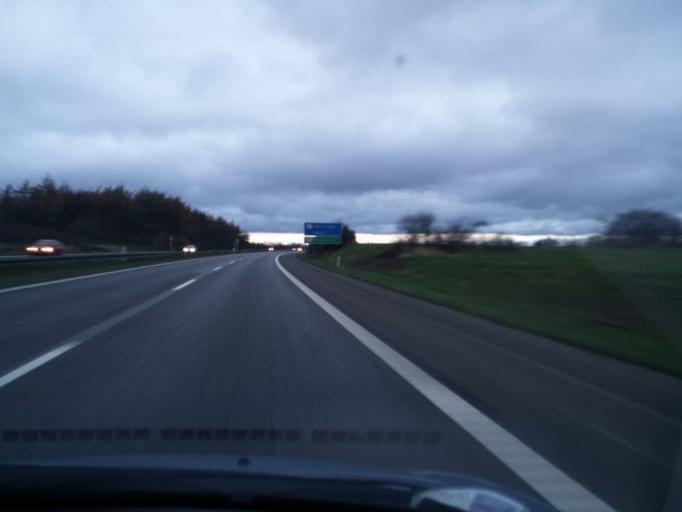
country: DK
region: South Denmark
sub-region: Middelfart Kommune
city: Norre Aby
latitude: 55.4636
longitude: 9.9108
